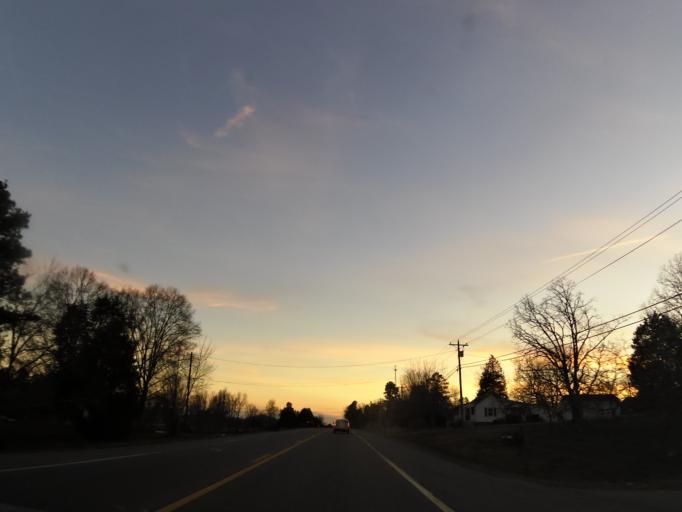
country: US
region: Tennessee
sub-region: Bradley County
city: Wildwood Lake
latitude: 35.0740
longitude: -84.8930
